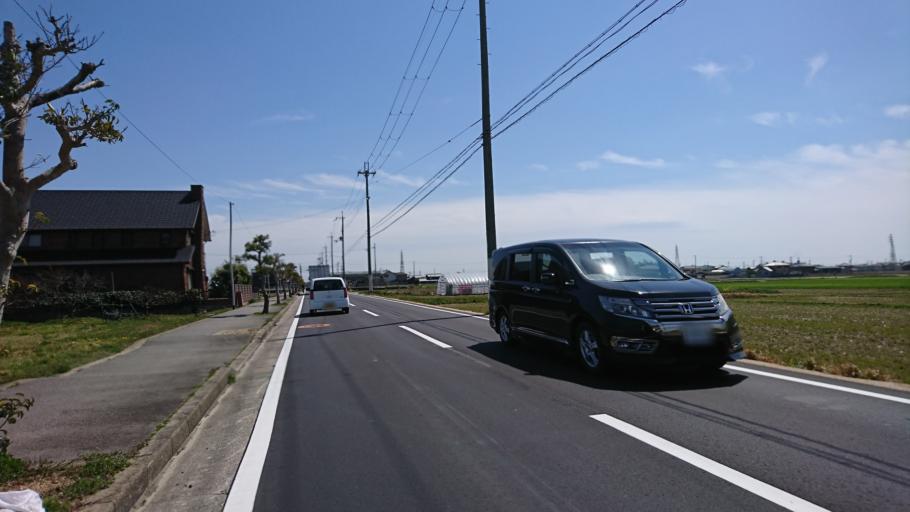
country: JP
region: Hyogo
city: Kakogawacho-honmachi
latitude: 34.7373
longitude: 134.8963
